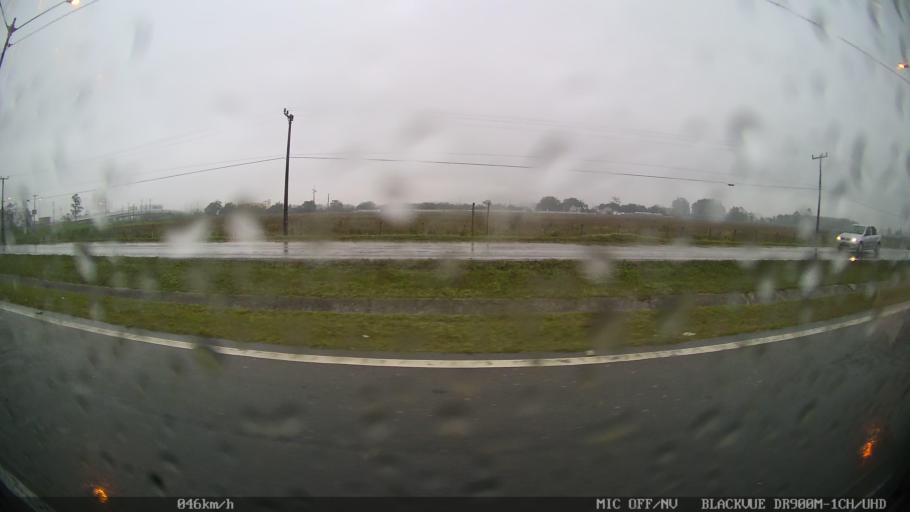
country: BR
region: Santa Catarina
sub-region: Navegantes
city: Navegantes
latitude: -26.8405
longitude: -48.7172
